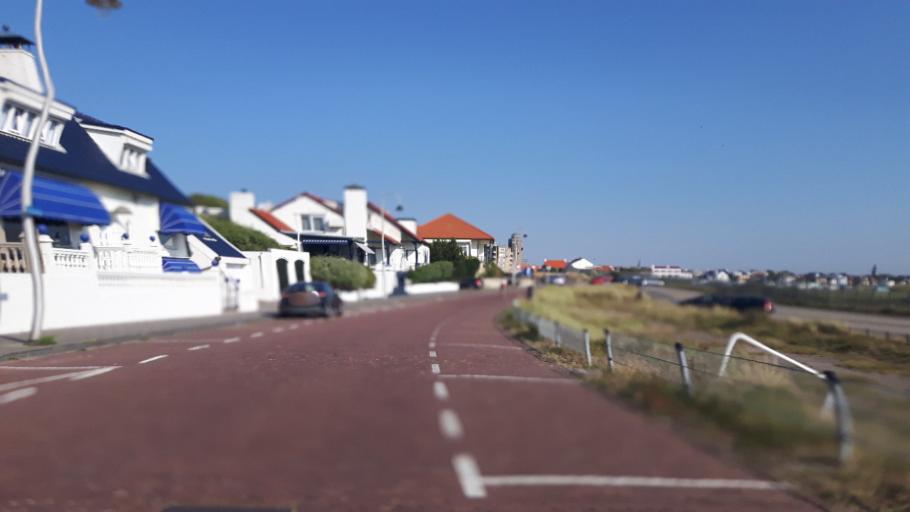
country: NL
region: North Holland
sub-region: Gemeente Zandvoort
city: Zandvoort
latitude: 52.3640
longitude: 4.5203
